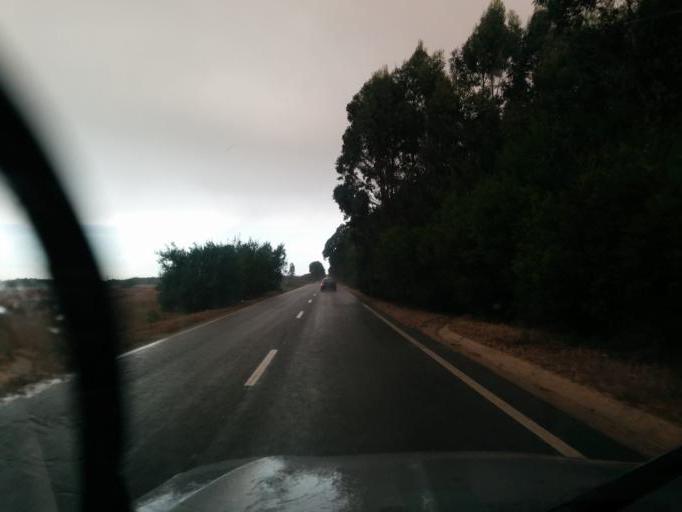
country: PT
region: Beja
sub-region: Odemira
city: Vila Nova de Milfontes
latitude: 37.6855
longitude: -8.7649
